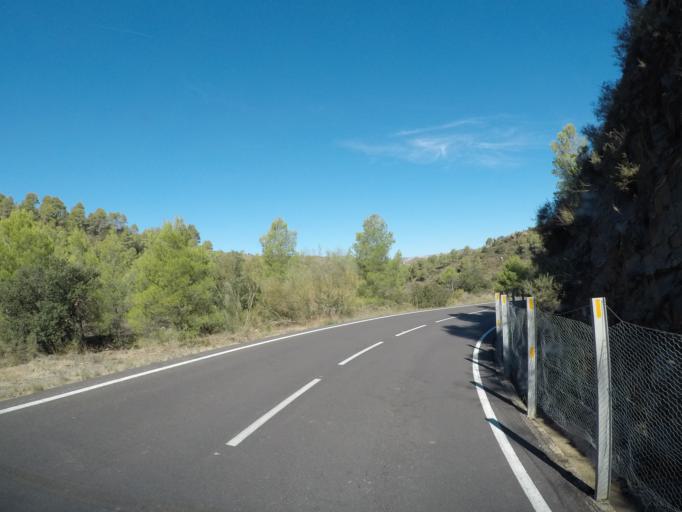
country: ES
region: Catalonia
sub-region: Provincia de Tarragona
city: Falset
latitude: 41.1713
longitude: 0.7984
